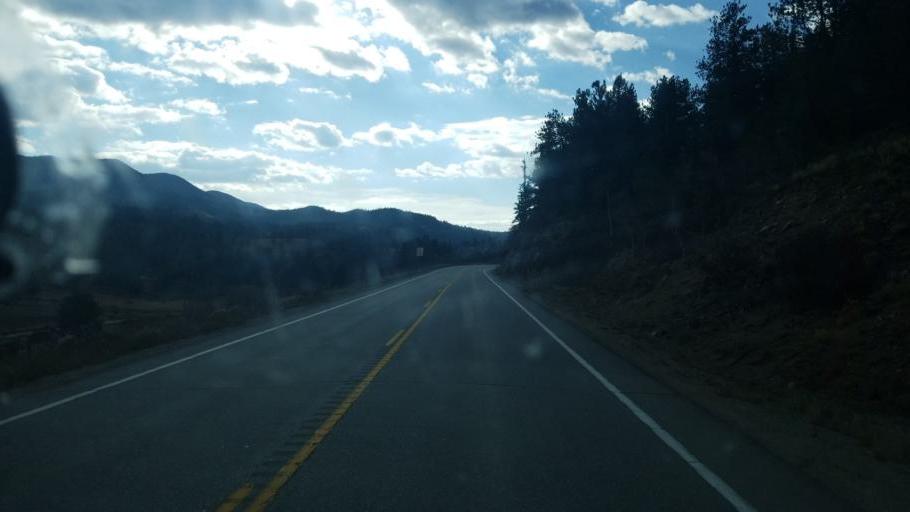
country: US
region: Colorado
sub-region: Chaffee County
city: Buena Vista
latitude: 38.8552
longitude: -105.9852
